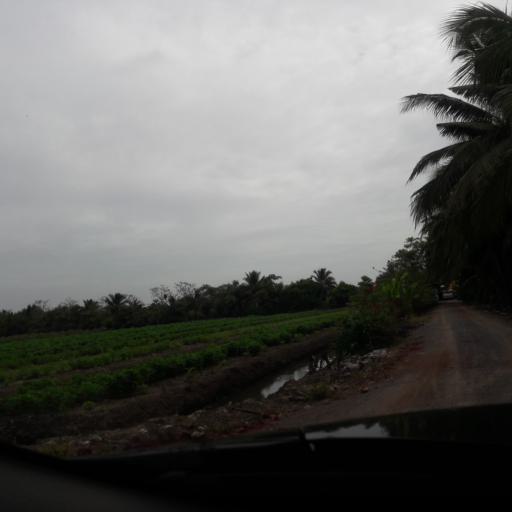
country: TH
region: Ratchaburi
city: Damnoen Saduak
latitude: 13.5662
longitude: 99.9444
